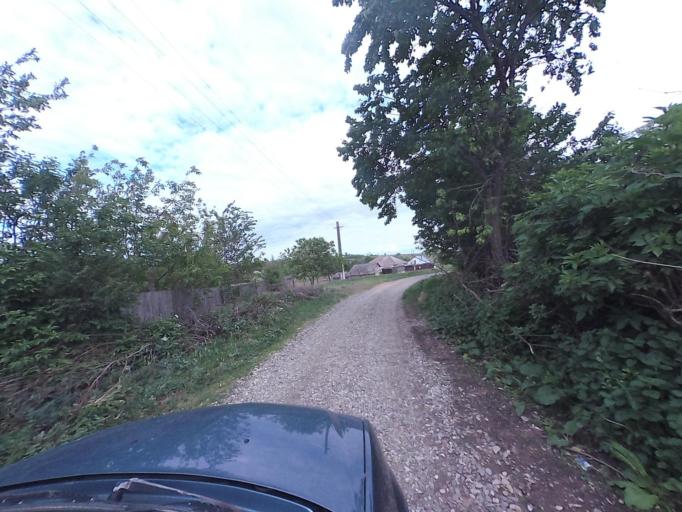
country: RO
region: Neamt
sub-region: Comuna Dulcesti
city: Dulcesti
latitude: 46.9554
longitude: 26.7934
